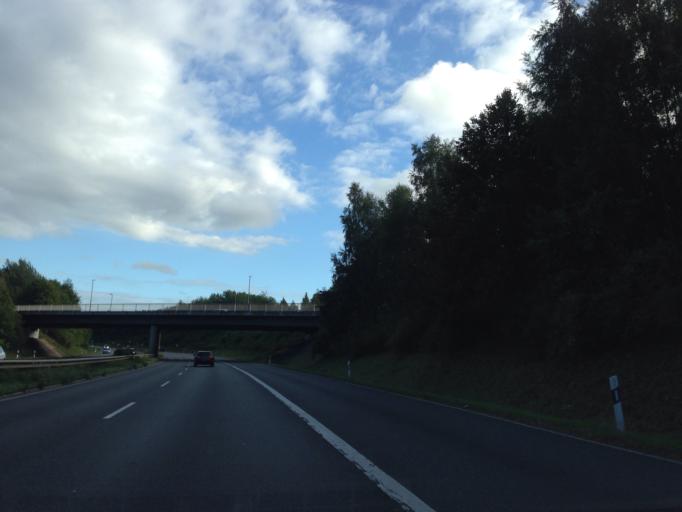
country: DE
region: Lower Saxony
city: Lueneburg
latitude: 53.2518
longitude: 10.4447
